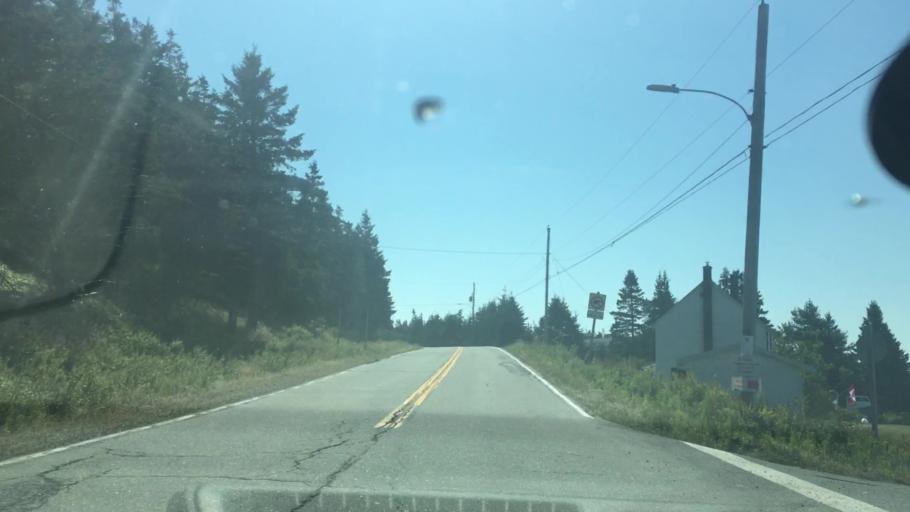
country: CA
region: Nova Scotia
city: New Glasgow
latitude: 44.9126
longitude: -62.3798
